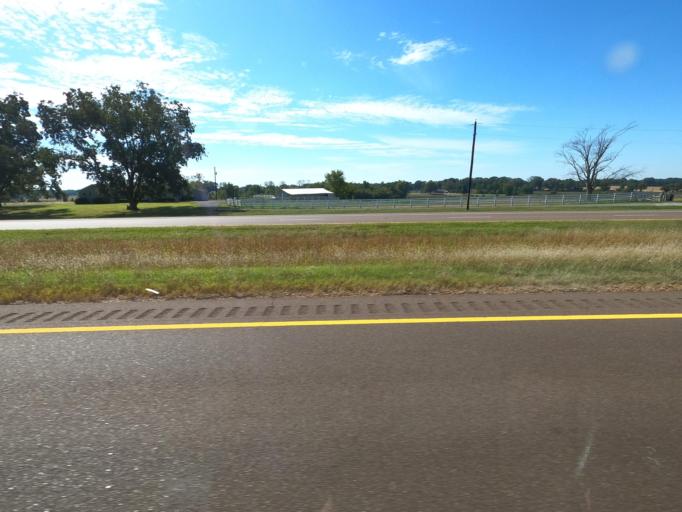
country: US
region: Tennessee
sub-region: Dyer County
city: Dyersburg
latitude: 35.9514
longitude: -89.3134
